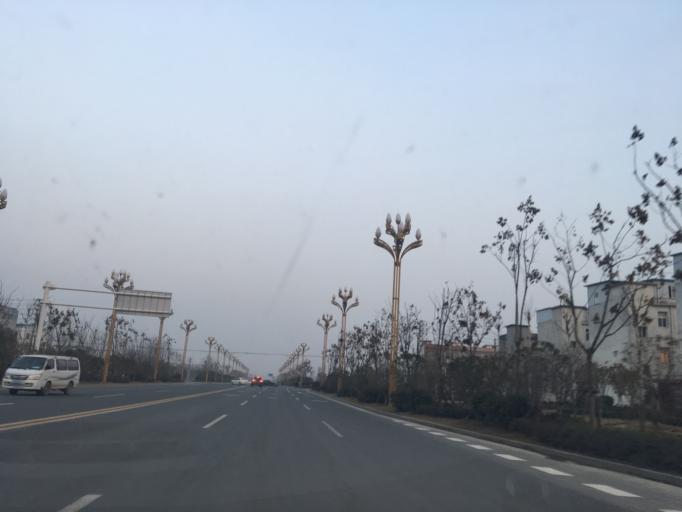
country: CN
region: Hubei
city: Macheng
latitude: 31.1612
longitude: 115.0194
